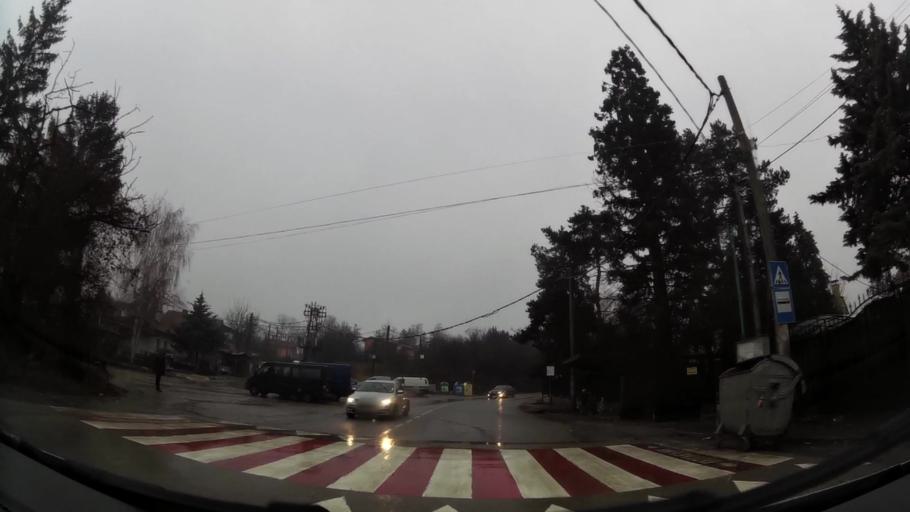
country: BG
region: Sofia-Capital
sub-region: Stolichna Obshtina
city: Sofia
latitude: 42.6267
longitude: 23.3586
